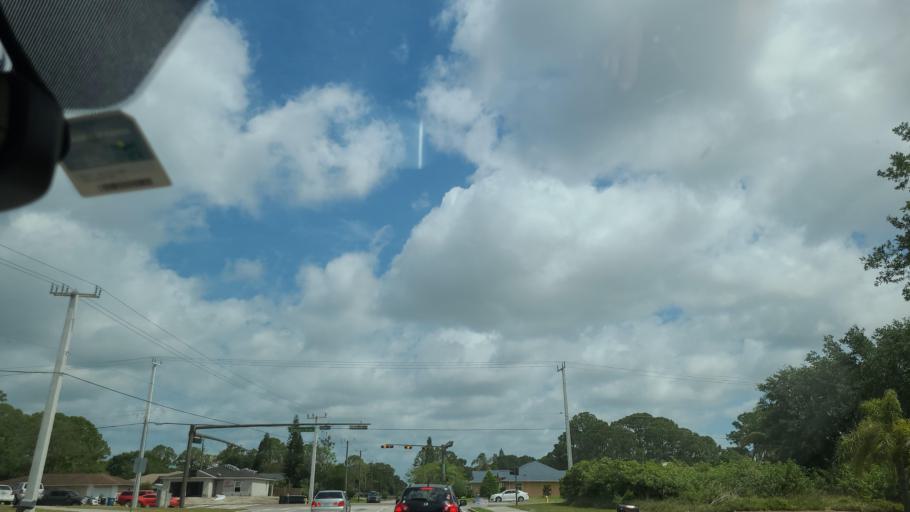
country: US
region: Florida
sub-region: Brevard County
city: June Park
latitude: 28.0311
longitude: -80.6958
